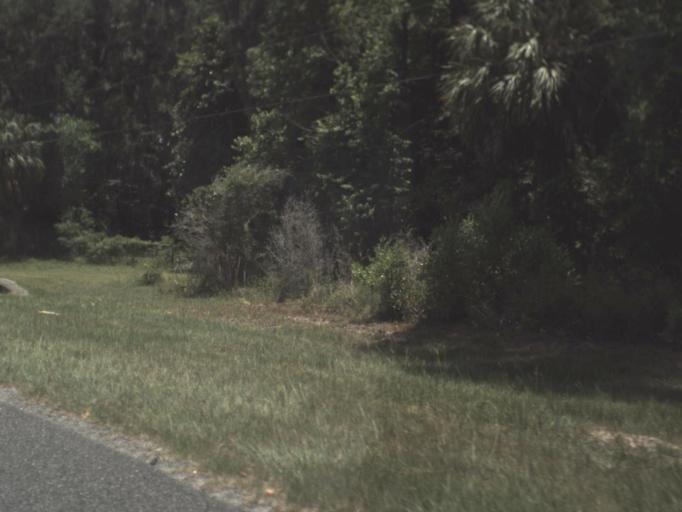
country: US
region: Florida
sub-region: Dixie County
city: Cross City
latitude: 29.6037
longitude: -83.0278
